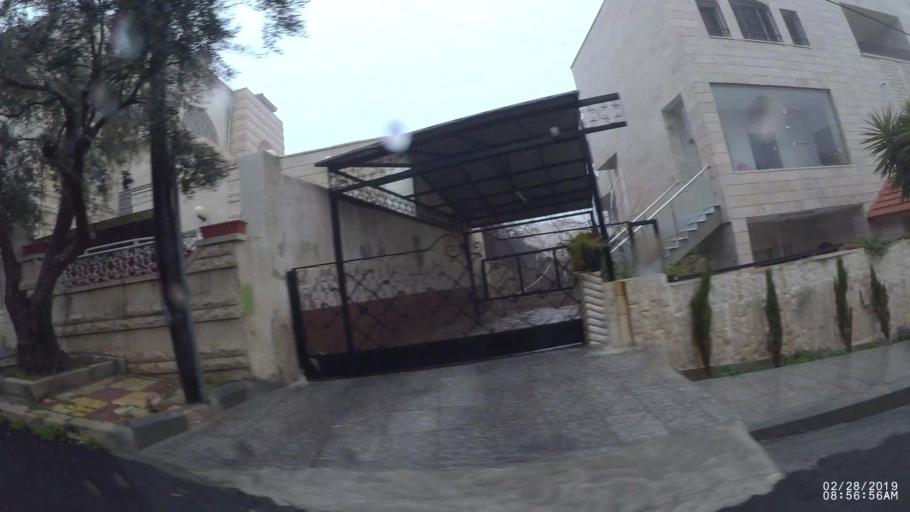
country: JO
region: Amman
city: Al Jubayhah
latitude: 32.0204
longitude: 35.8803
